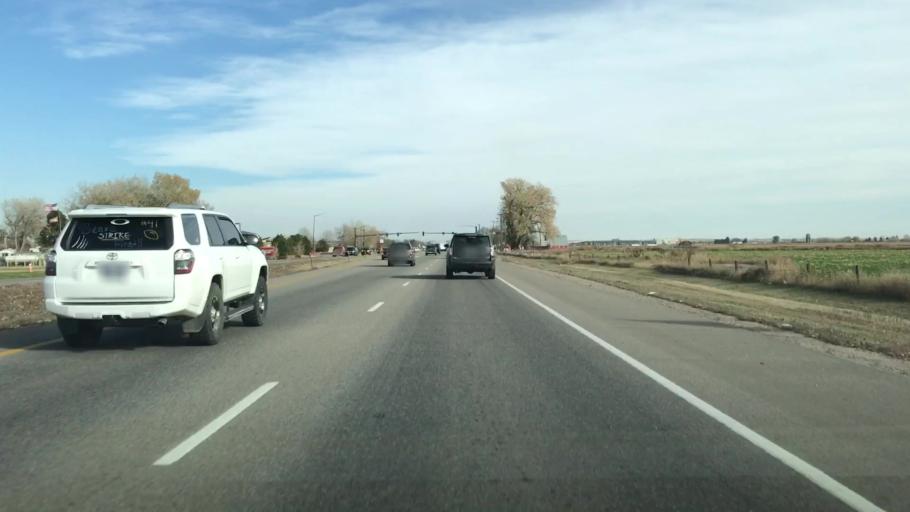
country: US
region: Colorado
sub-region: Larimer County
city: Loveland
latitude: 40.4071
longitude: -105.0150
